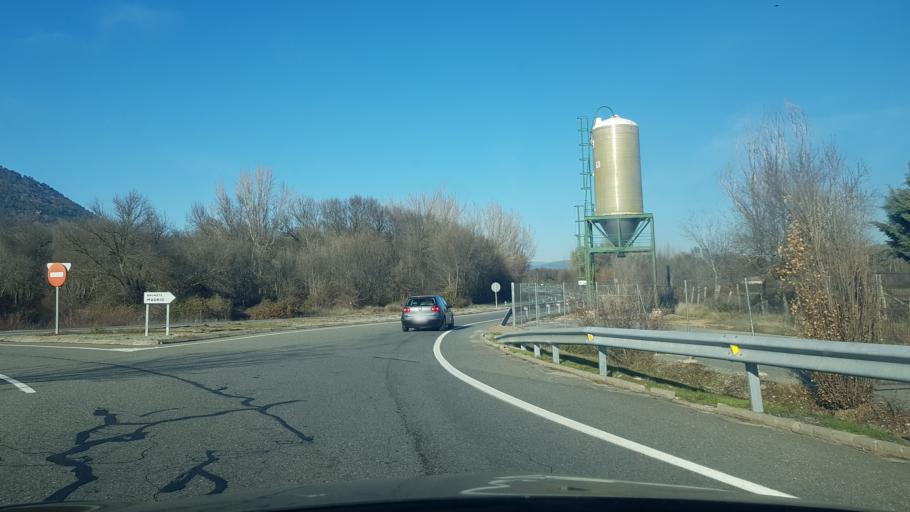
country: ES
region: Madrid
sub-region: Provincia de Madrid
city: Cadalso de los Vidrios
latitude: 40.3457
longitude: -4.4430
